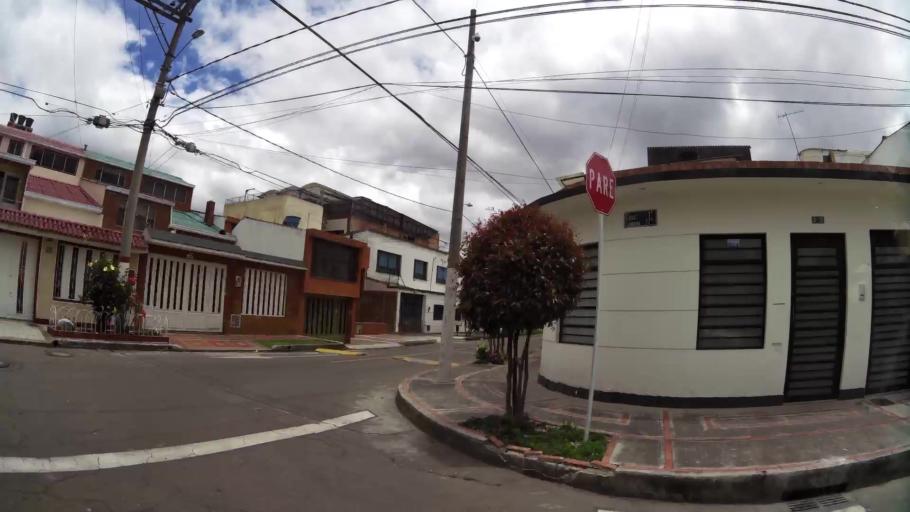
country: CO
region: Bogota D.C.
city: Bogota
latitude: 4.6045
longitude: -74.1115
